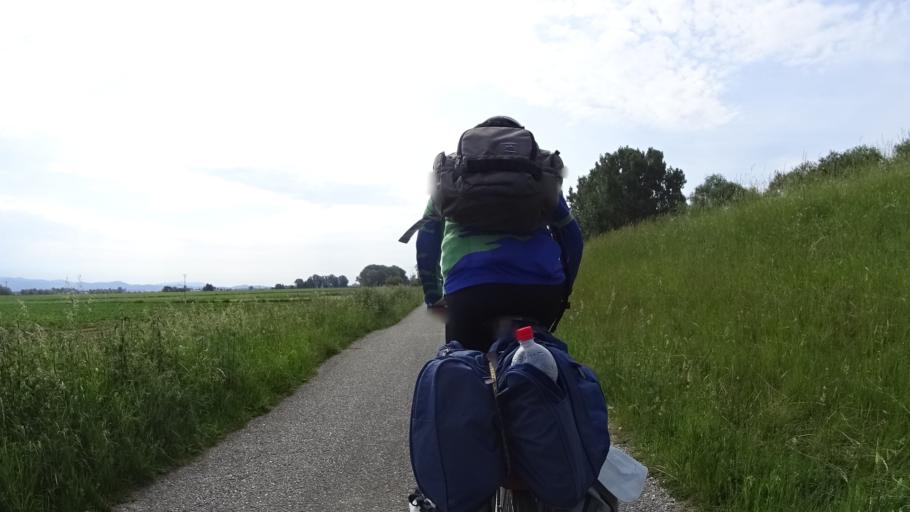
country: DE
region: Bavaria
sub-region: Lower Bavaria
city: Irlbach
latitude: 48.8385
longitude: 12.7743
